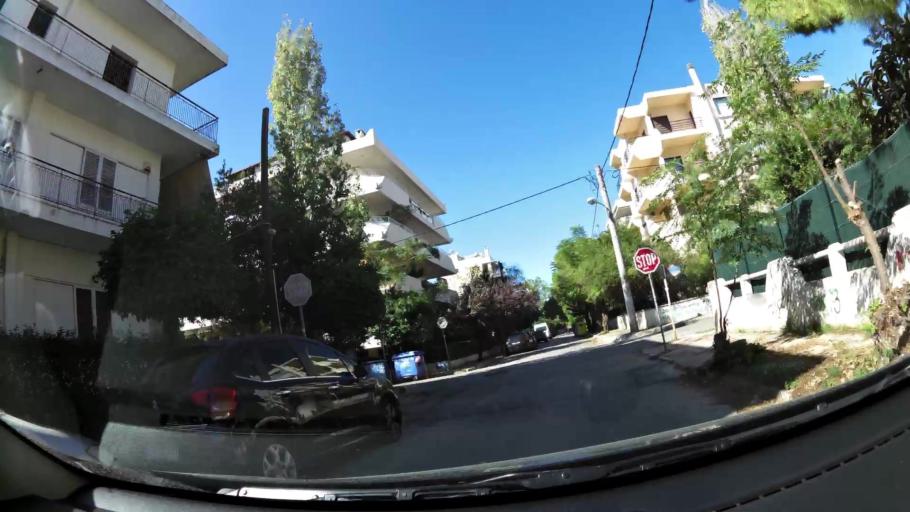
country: GR
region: Attica
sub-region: Nomarchia Athinas
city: Khalandrion
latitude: 38.0270
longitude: 23.8061
